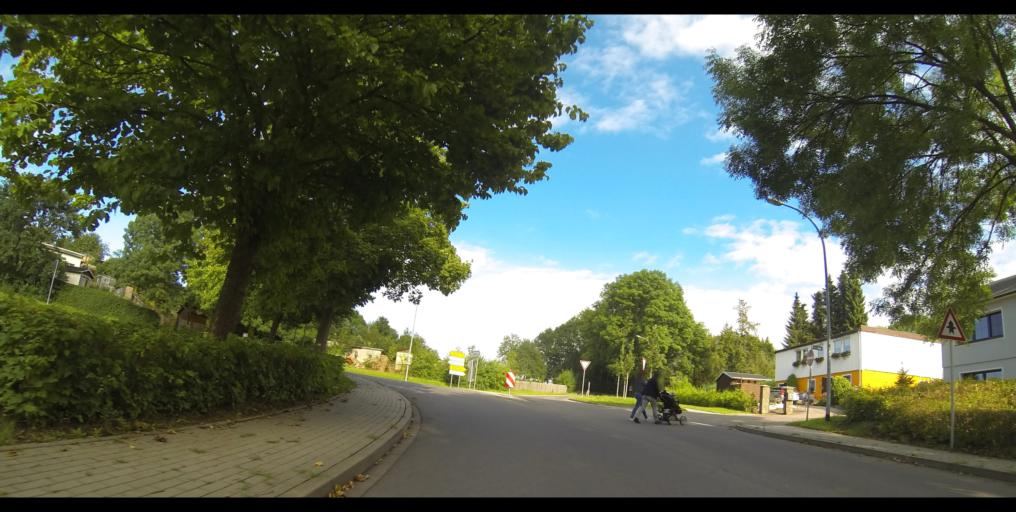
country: DE
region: Saxony
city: Hainichen
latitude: 50.9718
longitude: 13.1290
